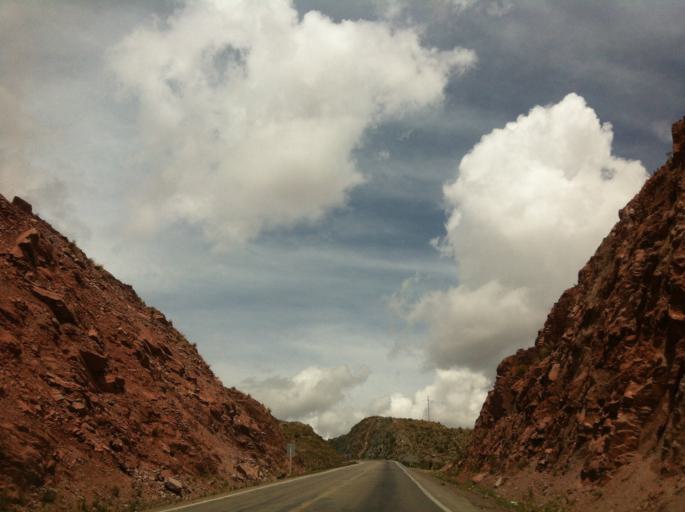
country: BO
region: Cochabamba
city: Sipe Sipe
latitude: -17.7076
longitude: -66.6788
